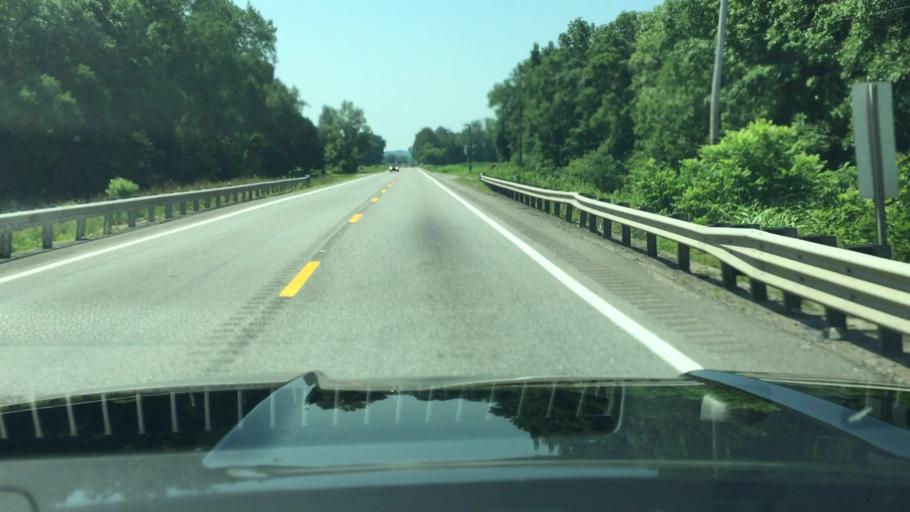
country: US
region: West Virginia
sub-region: Putnam County
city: Buffalo
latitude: 38.6901
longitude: -81.9652
